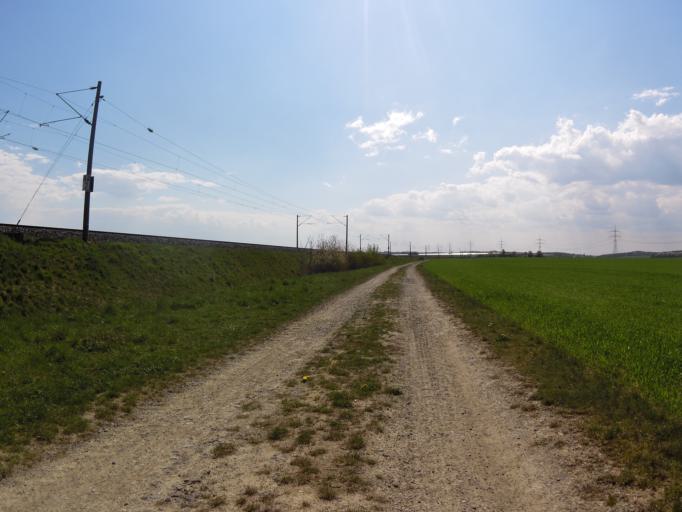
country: DE
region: Bavaria
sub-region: Regierungsbezirk Unterfranken
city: Oberpleichfeld
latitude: 49.8421
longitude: 10.1008
